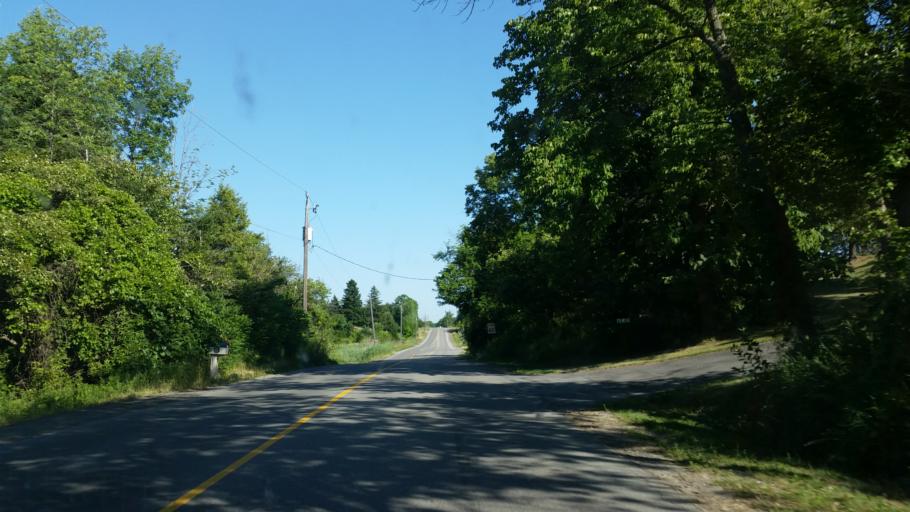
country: CA
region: Ontario
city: Bradford West Gwillimbury
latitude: 43.9497
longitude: -79.7629
